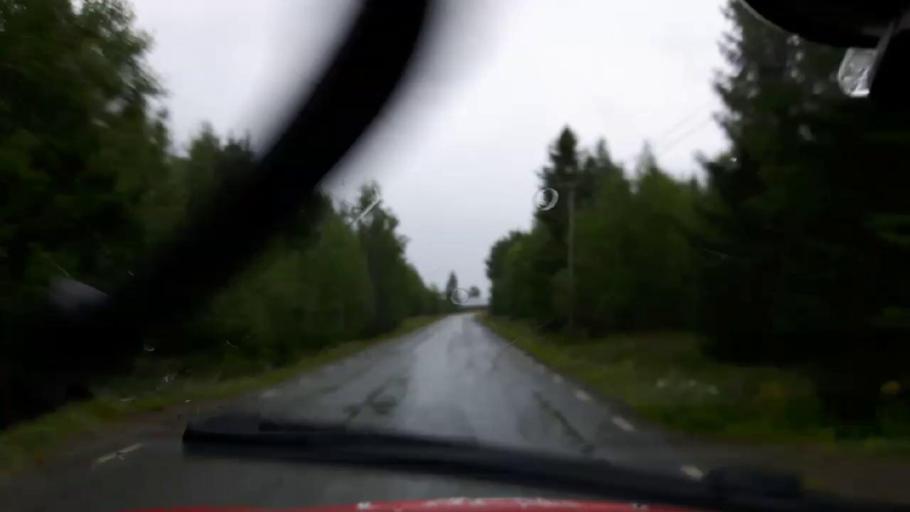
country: SE
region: Jaemtland
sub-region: OEstersunds Kommun
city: Brunflo
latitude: 62.9897
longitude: 14.8016
